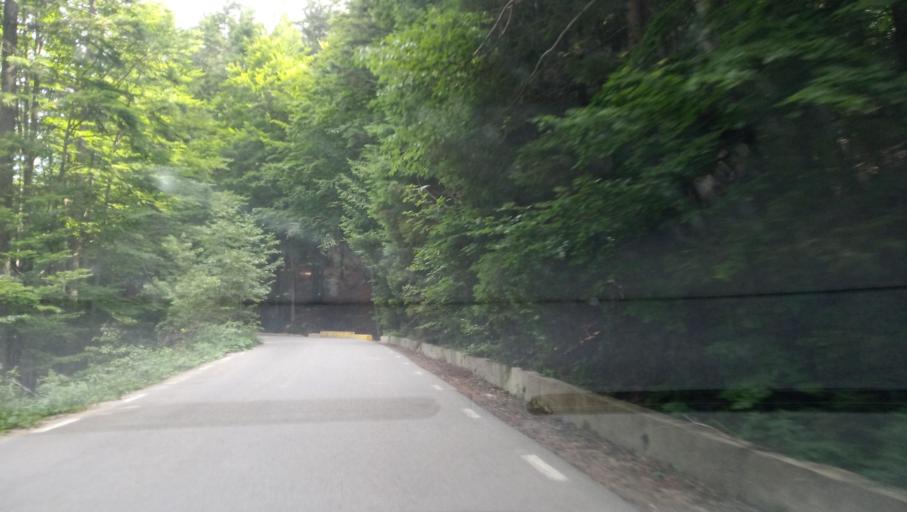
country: RO
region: Prahova
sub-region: Oras Sinaia
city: Sinaia
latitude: 45.3200
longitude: 25.5153
